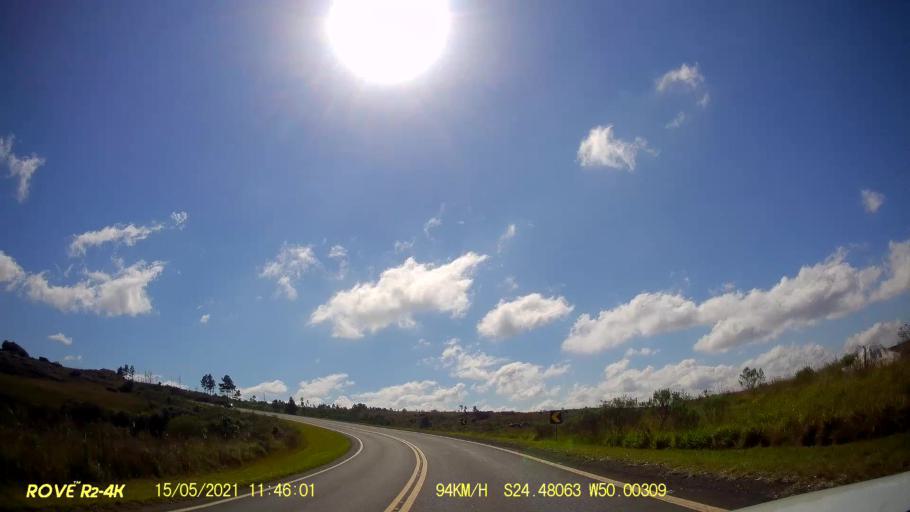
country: BR
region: Parana
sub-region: Pirai Do Sul
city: Pirai do Sul
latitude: -24.4805
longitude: -50.0033
